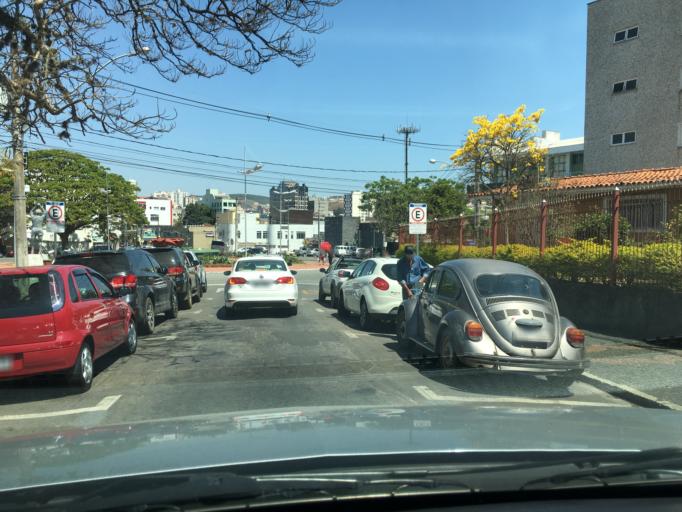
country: BR
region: Minas Gerais
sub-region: Pocos De Caldas
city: Pocos de Caldas
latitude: -21.7847
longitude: -46.5616
